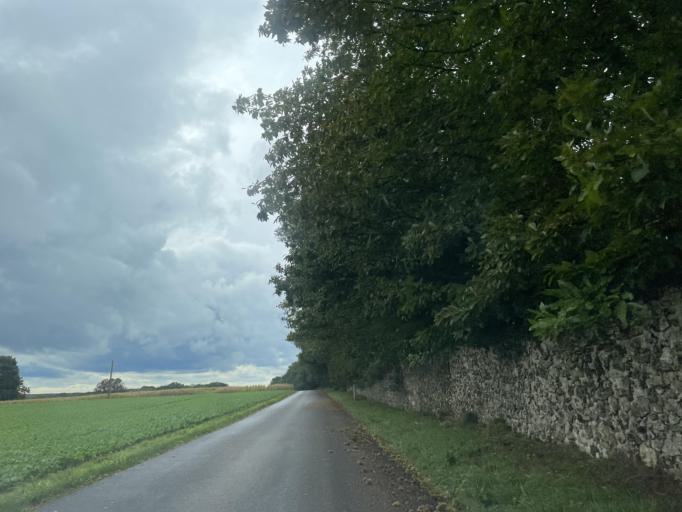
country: FR
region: Ile-de-France
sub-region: Departement de Seine-et-Marne
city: Trilport
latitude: 48.9373
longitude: 2.9837
